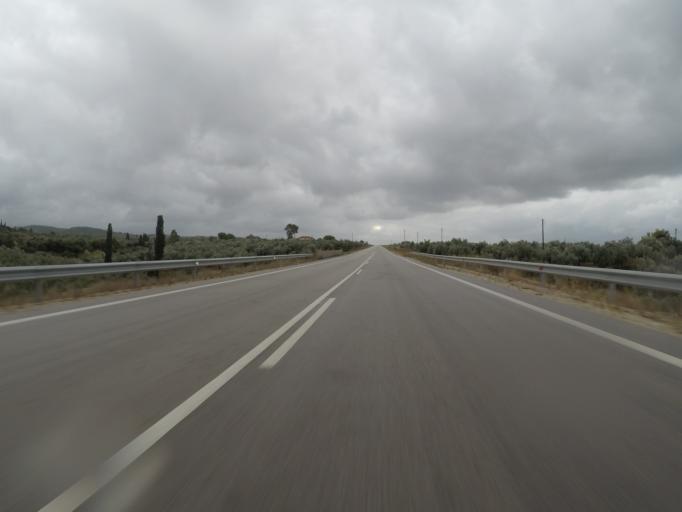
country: GR
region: Peloponnese
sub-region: Nomos Messinias
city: Gargalianoi
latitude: 37.0202
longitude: 21.6387
